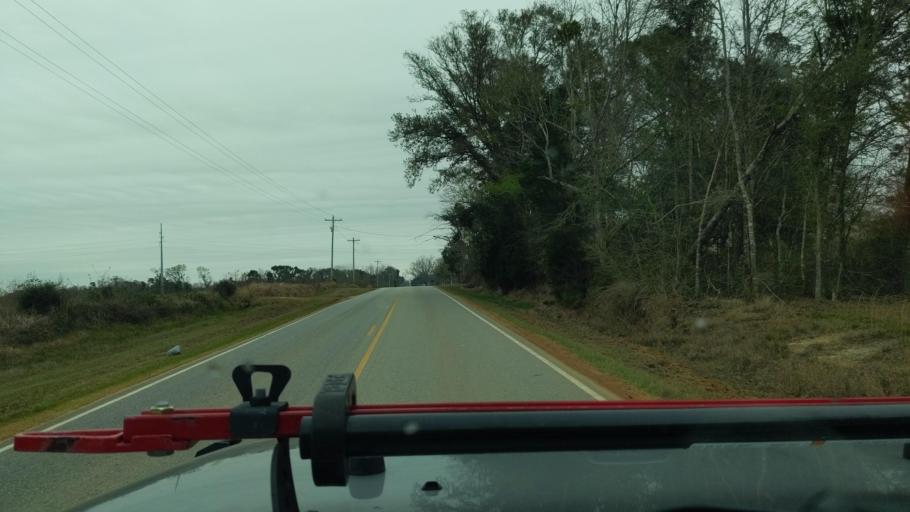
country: US
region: Alabama
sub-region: Baldwin County
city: Foley
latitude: 30.4579
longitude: -87.7553
